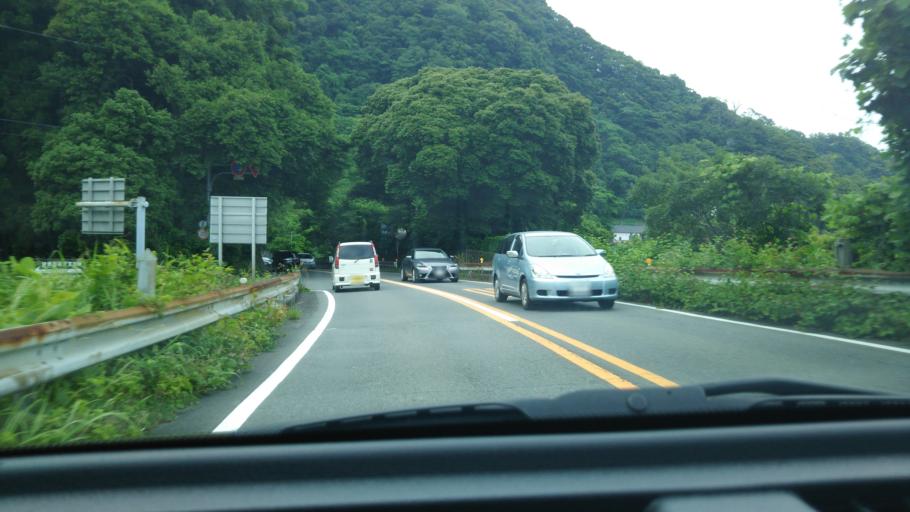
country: JP
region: Shizuoka
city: Ito
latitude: 34.8706
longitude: 139.0960
